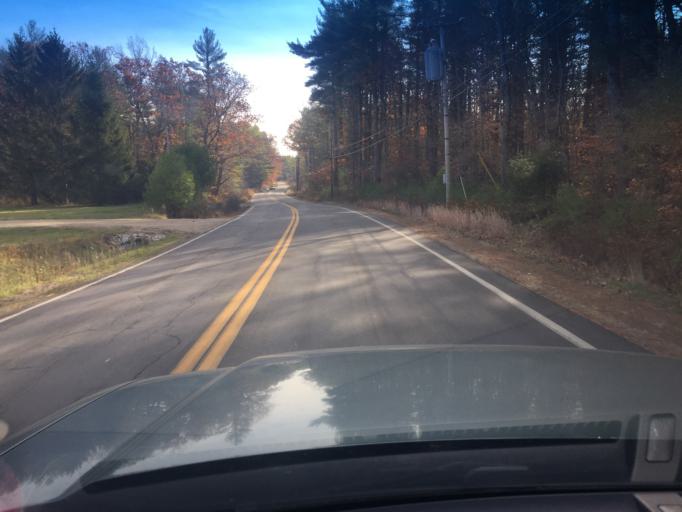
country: US
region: Maine
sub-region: York County
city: Eliot
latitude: 43.1757
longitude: -70.7240
